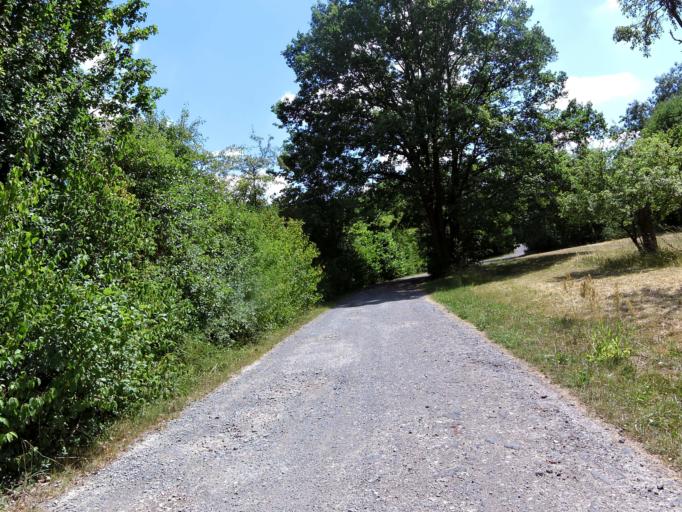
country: DE
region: Bavaria
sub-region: Regierungsbezirk Unterfranken
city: Gerbrunn
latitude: 49.7859
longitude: 9.9961
